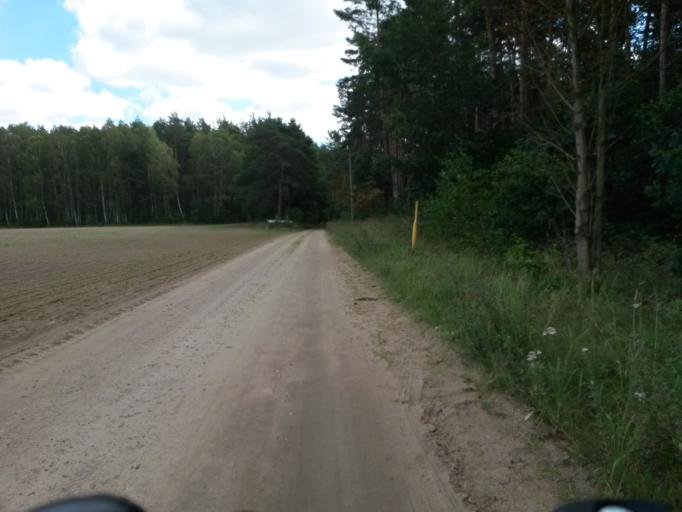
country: DE
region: Brandenburg
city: Templin
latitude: 53.1707
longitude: 13.4596
